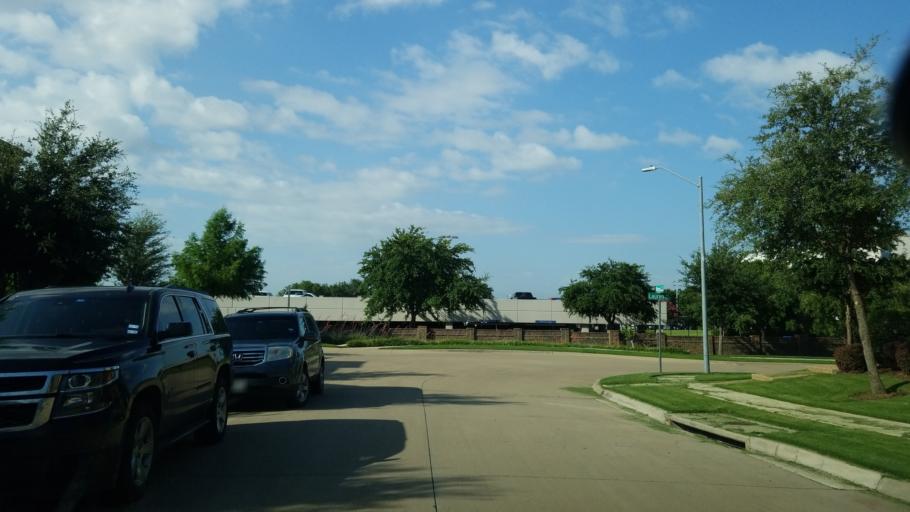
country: US
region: Texas
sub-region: Dallas County
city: Coppell
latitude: 32.9216
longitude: -96.9689
